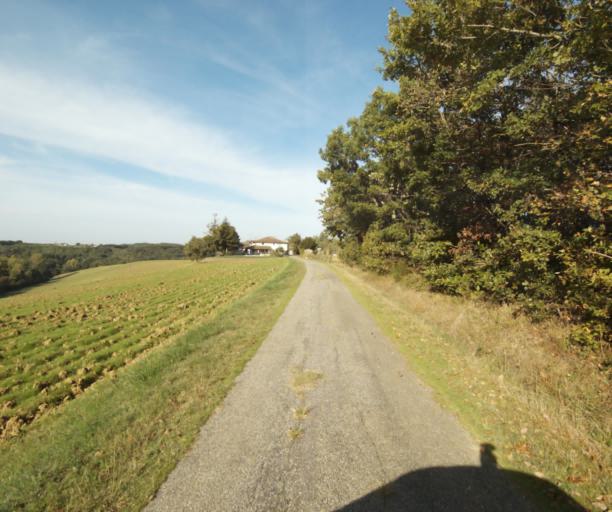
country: FR
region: Midi-Pyrenees
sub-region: Departement du Tarn-et-Garonne
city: Nohic
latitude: 43.9304
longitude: 1.4542
